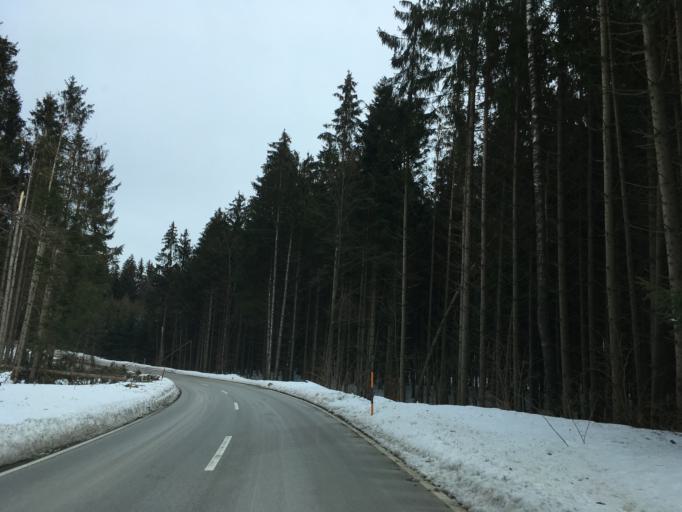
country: DE
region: Bavaria
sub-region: Upper Bavaria
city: Schnaitsee
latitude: 48.0558
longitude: 12.3523
